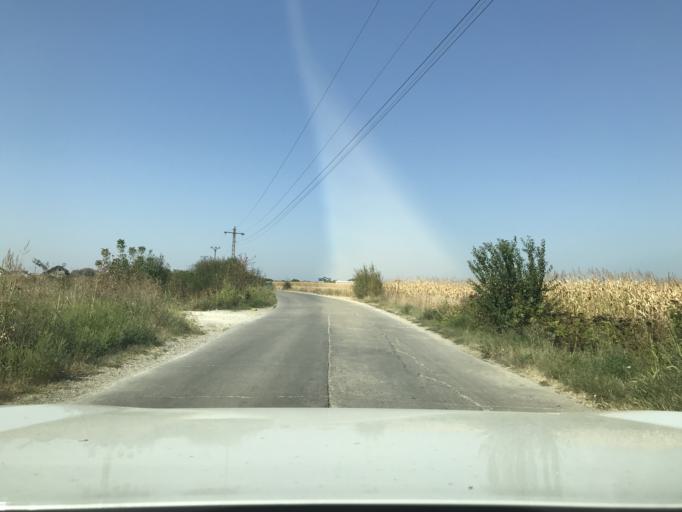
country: RO
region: Olt
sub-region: Comuna Slatioara
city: Slatioara
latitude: 44.3934
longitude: 24.3328
